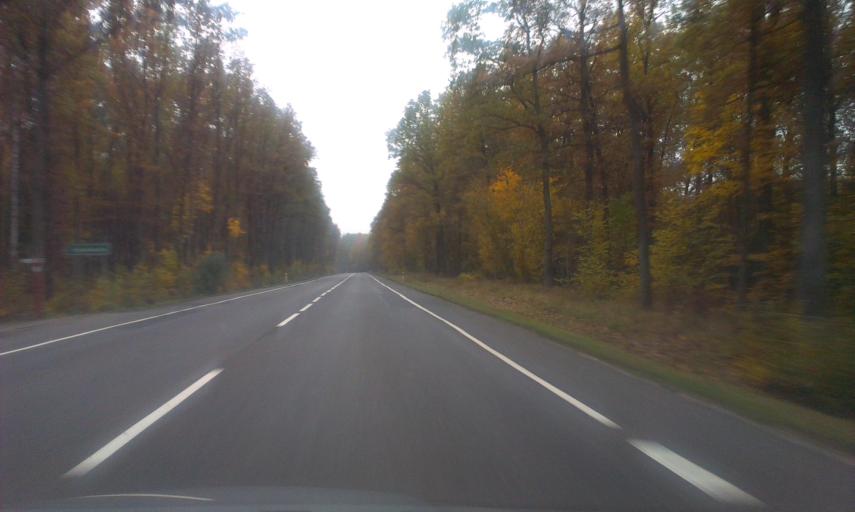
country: PL
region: Greater Poland Voivodeship
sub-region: Powiat chodzieski
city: Budzyn
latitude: 52.9178
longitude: 16.9713
